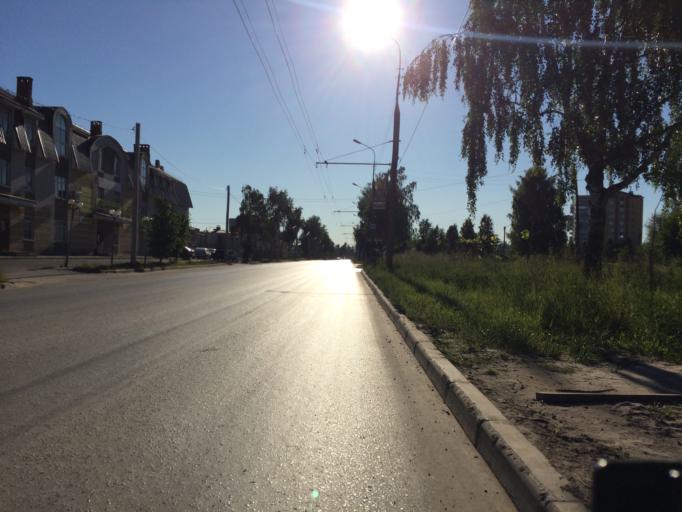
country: RU
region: Mariy-El
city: Yoshkar-Ola
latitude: 56.6534
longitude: 47.8667
